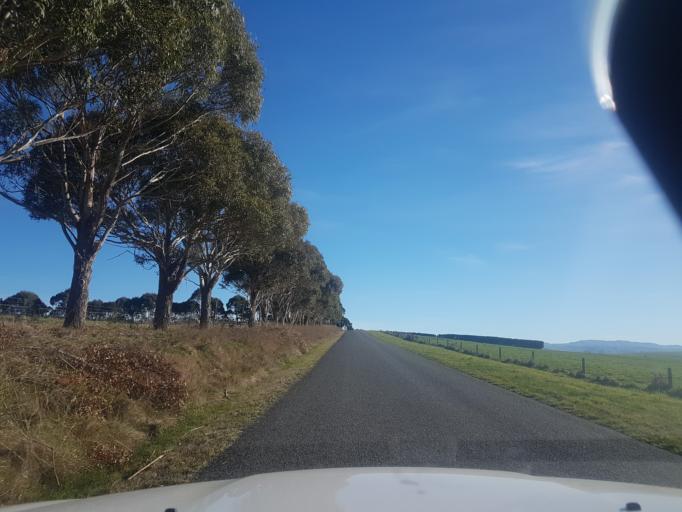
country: NZ
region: Canterbury
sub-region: Timaru District
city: Pleasant Point
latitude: -44.2476
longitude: 171.0774
